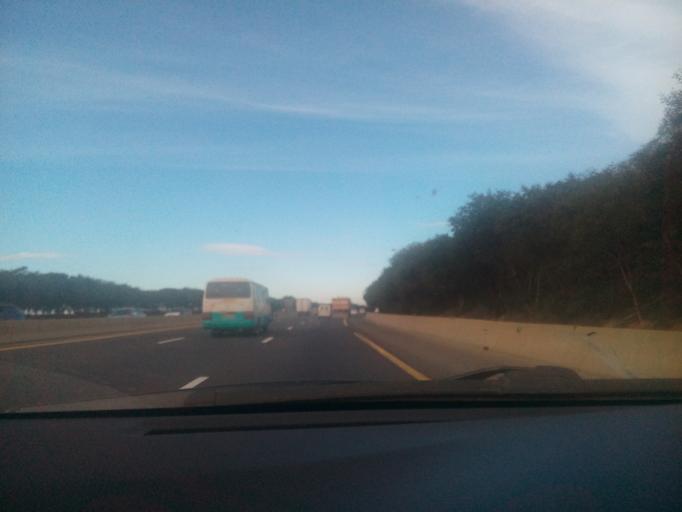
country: DZ
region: Oran
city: Es Senia
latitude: 35.5794
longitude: -0.5679
